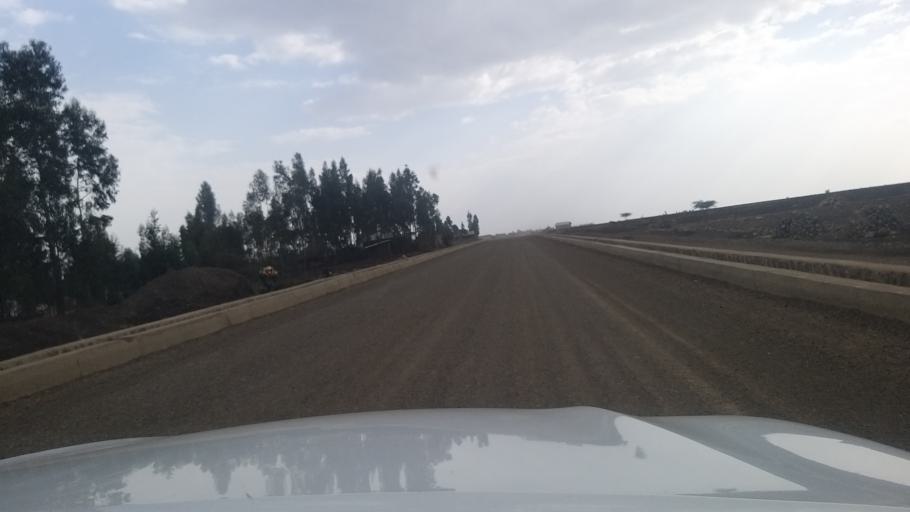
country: ET
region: Amhara
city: Were Ilu
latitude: 10.4484
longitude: 39.2019
